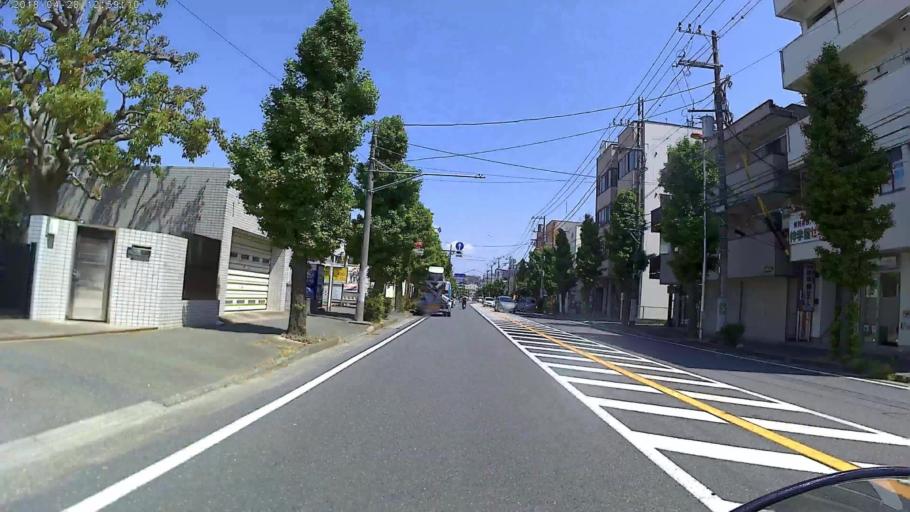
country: JP
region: Kanagawa
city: Yokosuka
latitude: 35.2539
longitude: 139.6727
